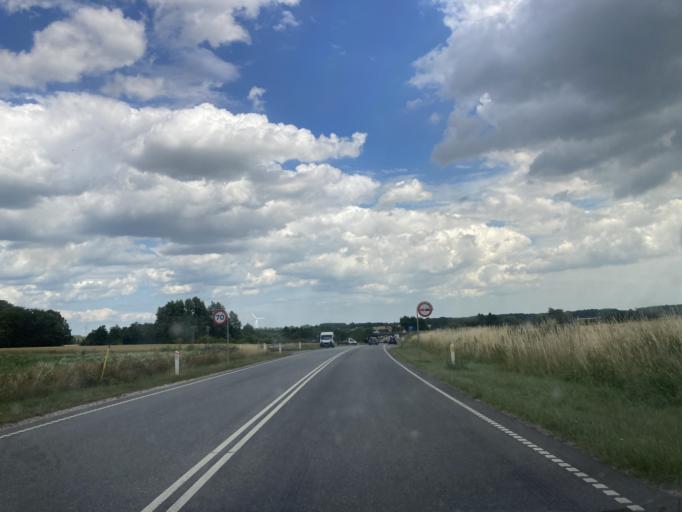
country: DK
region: Zealand
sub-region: Faxe Kommune
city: Haslev
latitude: 55.3404
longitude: 12.0393
